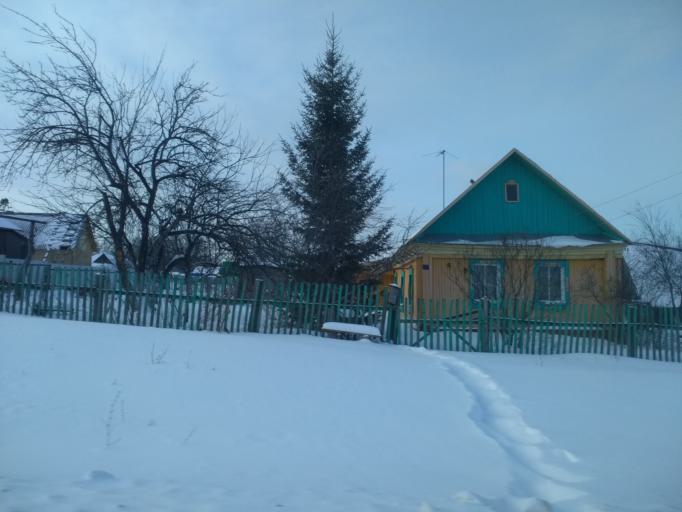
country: RU
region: Bashkortostan
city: Iglino
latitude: 54.7733
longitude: 56.5361
